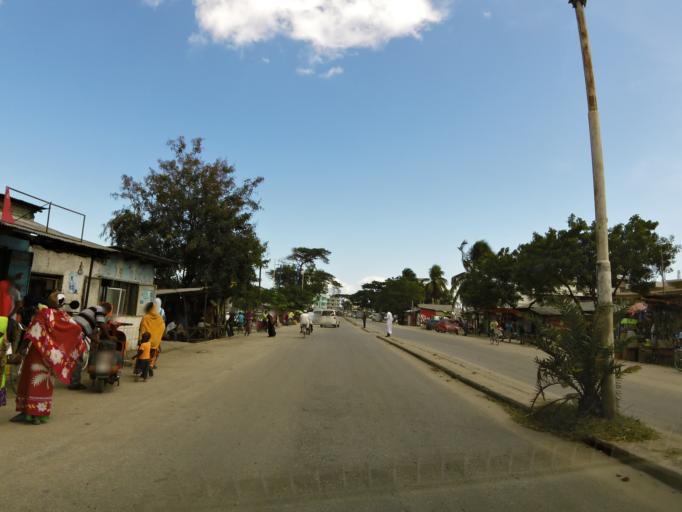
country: TZ
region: Zanzibar Urban/West
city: Zanzibar
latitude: -6.1634
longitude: 39.2152
